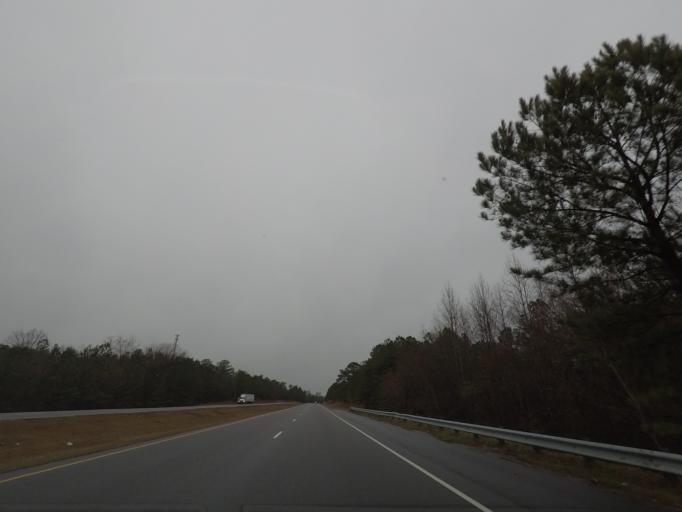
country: US
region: North Carolina
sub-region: Lee County
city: Broadway
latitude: 35.3402
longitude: -79.1010
